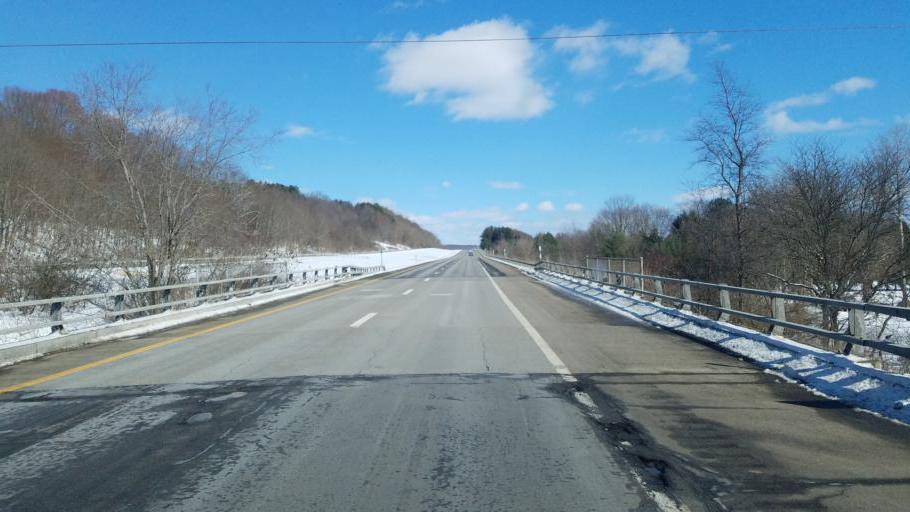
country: US
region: New York
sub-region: Chautauqua County
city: Falconer
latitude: 42.1361
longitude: -79.1274
